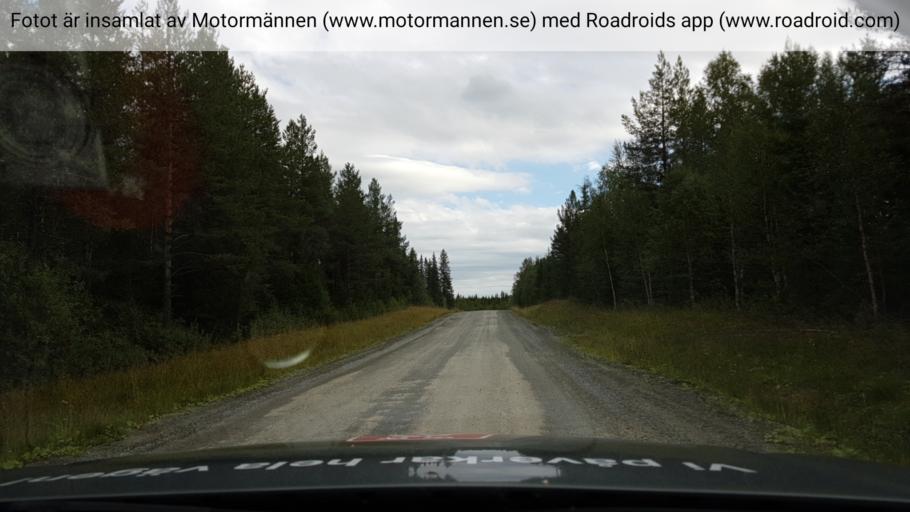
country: SE
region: Jaemtland
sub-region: Krokoms Kommun
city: Valla
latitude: 63.6593
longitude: 13.7600
